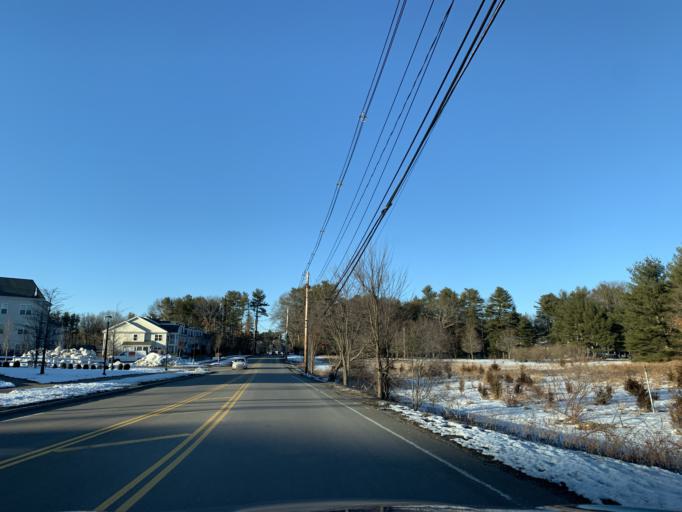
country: US
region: Massachusetts
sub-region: Bristol County
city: Norton Center
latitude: 41.9893
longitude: -71.1553
